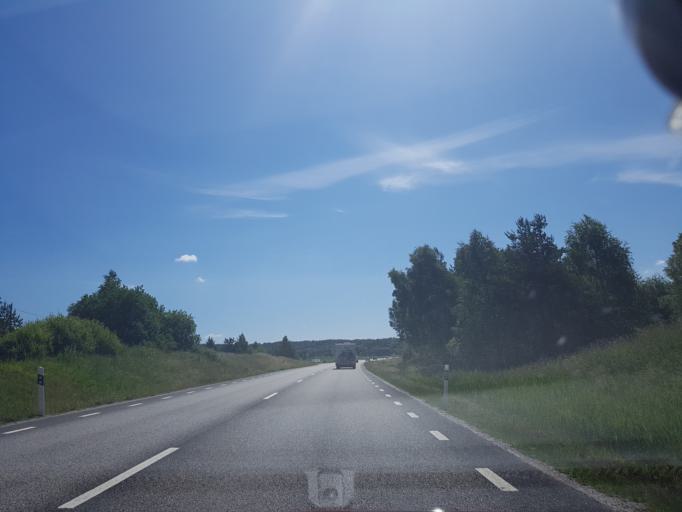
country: SE
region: Vaestra Goetaland
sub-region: Orust
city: Henan
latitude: 58.1444
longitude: 11.6365
